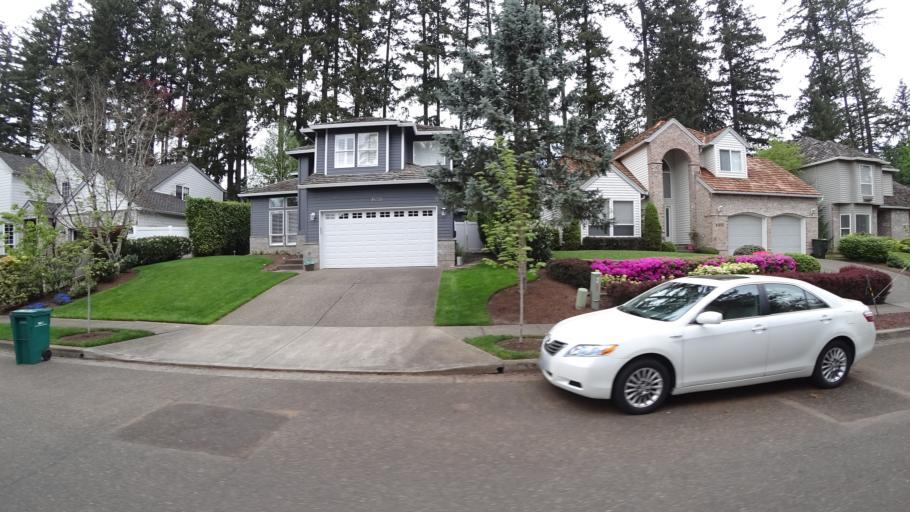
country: US
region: Oregon
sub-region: Washington County
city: Beaverton
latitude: 45.4500
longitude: -122.8335
